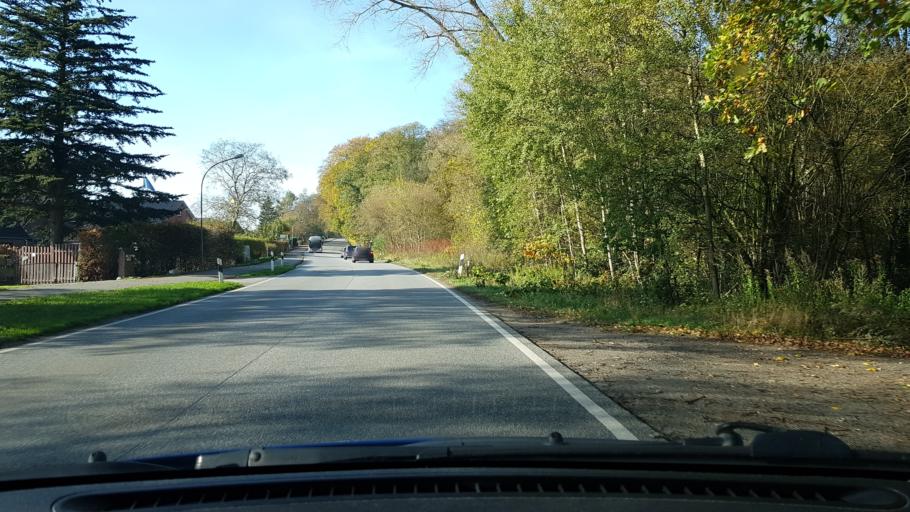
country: DE
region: Schleswig-Holstein
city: Escheburg
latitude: 53.4605
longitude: 10.3298
